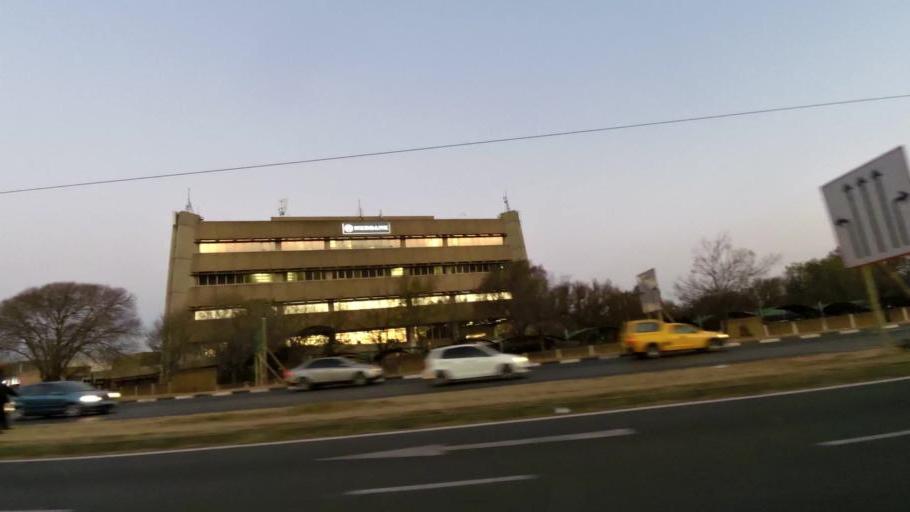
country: ZA
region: Gauteng
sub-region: City of Johannesburg Metropolitan Municipality
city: Johannesburg
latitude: -26.2144
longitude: 28.0144
